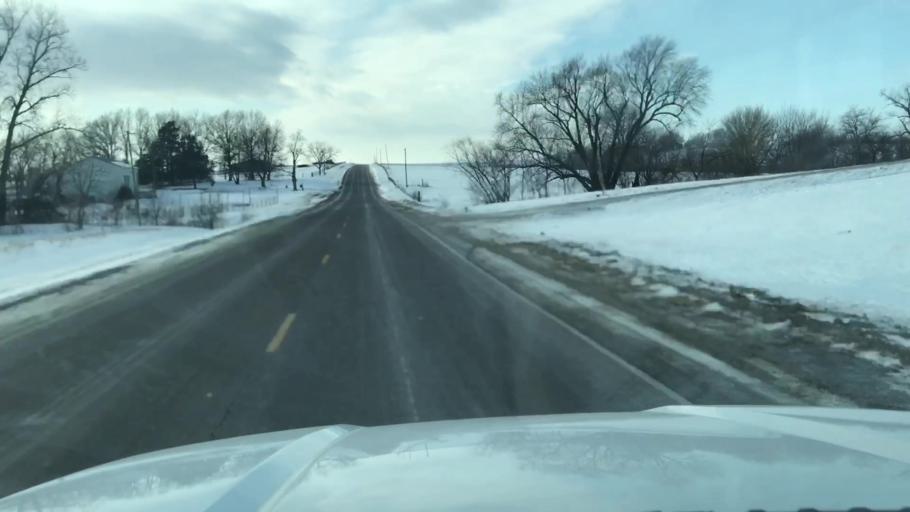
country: US
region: Missouri
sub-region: Nodaway County
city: Maryville
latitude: 40.2009
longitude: -94.8965
